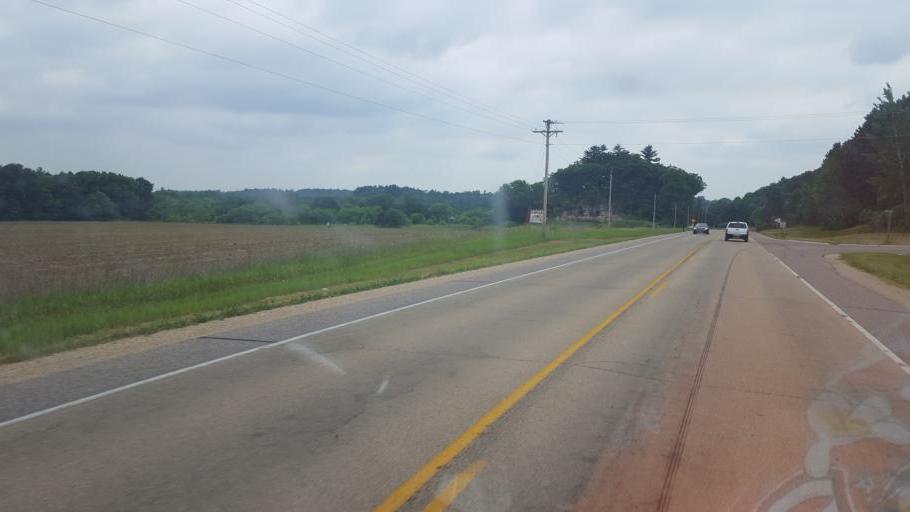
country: US
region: Wisconsin
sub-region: Juneau County
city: Elroy
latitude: 43.6379
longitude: -90.1820
